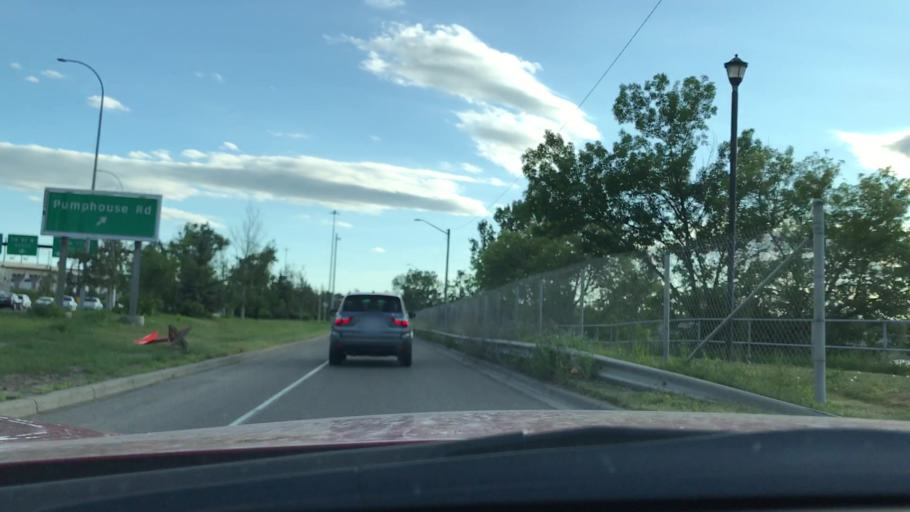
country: CA
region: Alberta
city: Calgary
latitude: 51.0480
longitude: -114.0908
